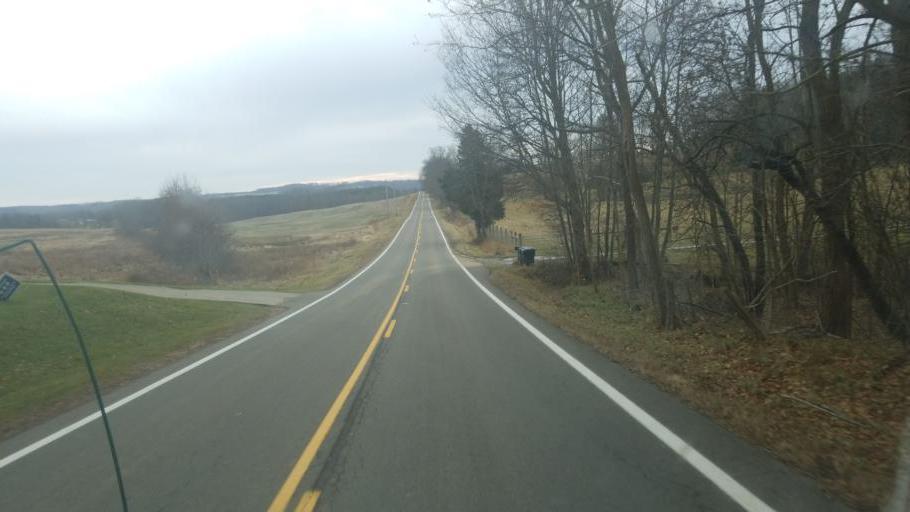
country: US
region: Ohio
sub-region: Sandusky County
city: Bellville
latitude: 40.6601
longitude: -82.3774
